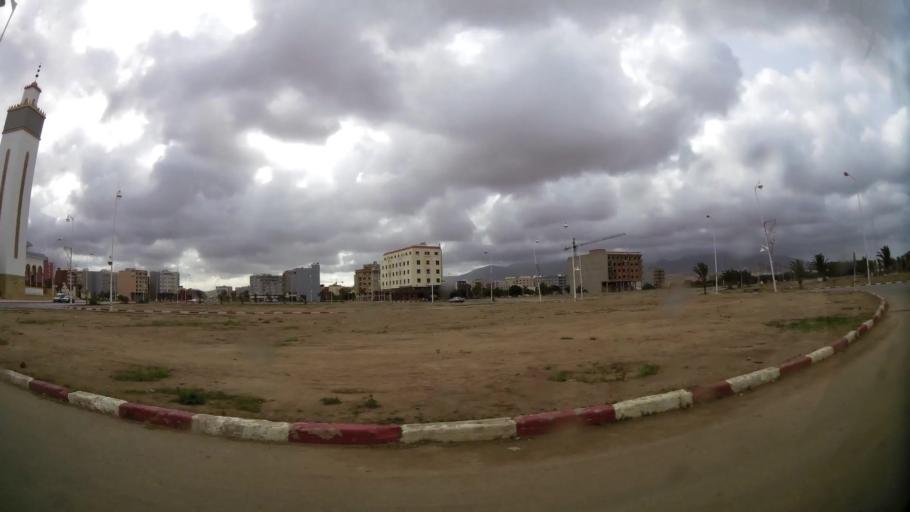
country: MA
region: Oriental
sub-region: Nador
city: Nador
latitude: 35.1532
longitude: -2.9182
